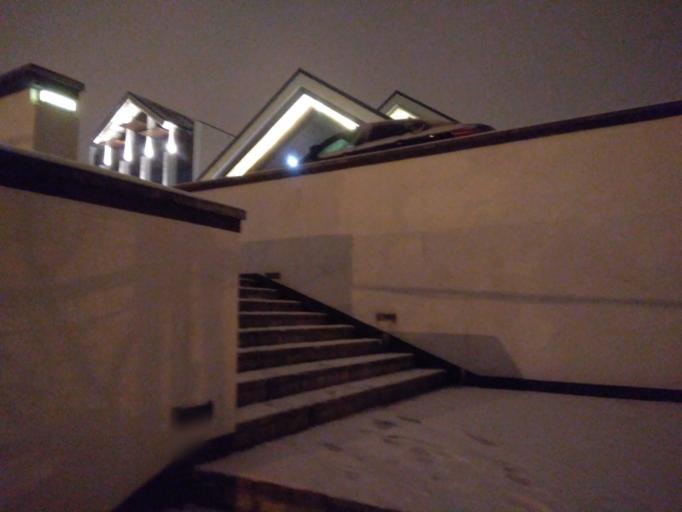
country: BY
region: Minsk
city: Minsk
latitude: 53.8927
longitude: 27.5789
